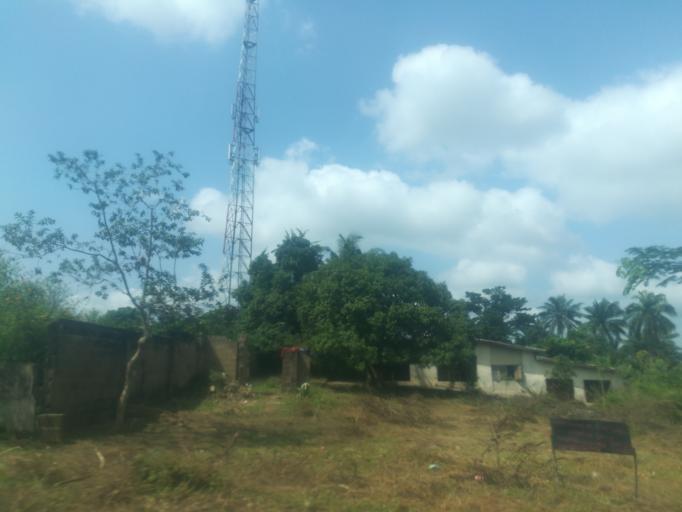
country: NG
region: Oyo
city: Moniya
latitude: 7.5478
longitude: 3.9105
